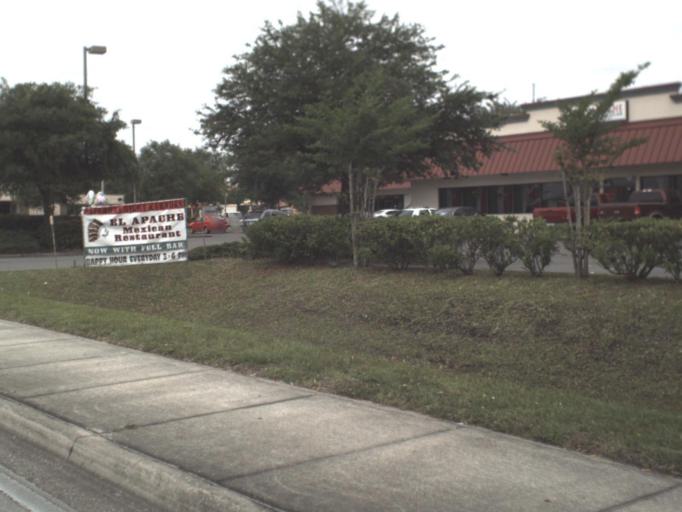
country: US
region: Florida
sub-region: Clay County
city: Lakeside
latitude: 30.1394
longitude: -81.7719
